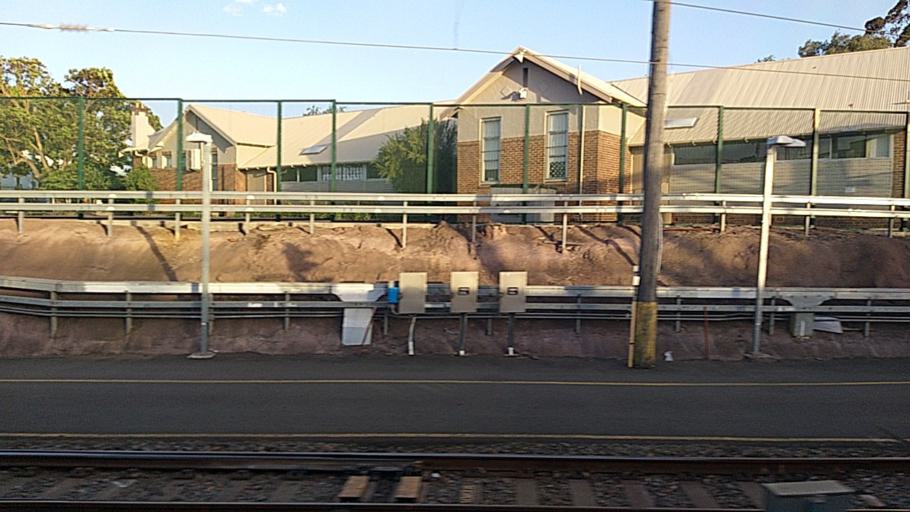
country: AU
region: New South Wales
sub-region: Hurstville
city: Penshurst
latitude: -33.9718
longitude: 151.0807
